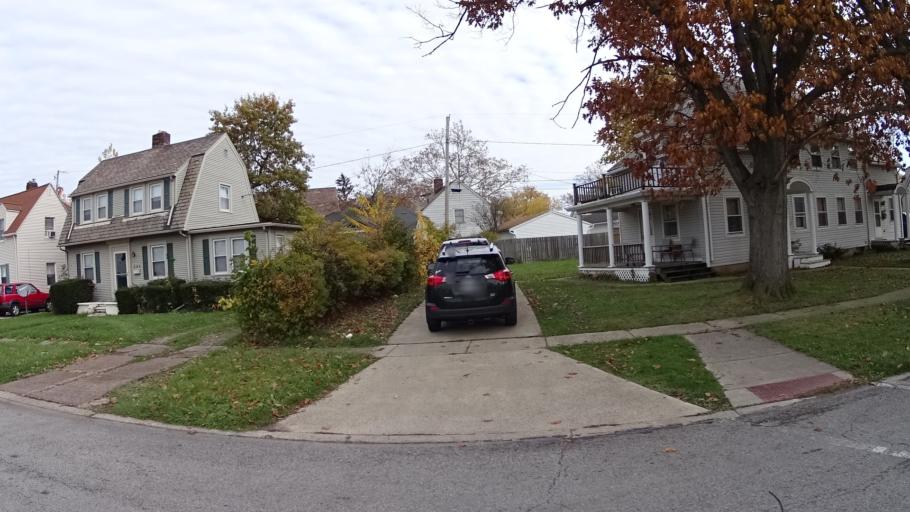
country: US
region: Ohio
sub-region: Lorain County
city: Lorain
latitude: 41.4730
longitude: -82.1591
